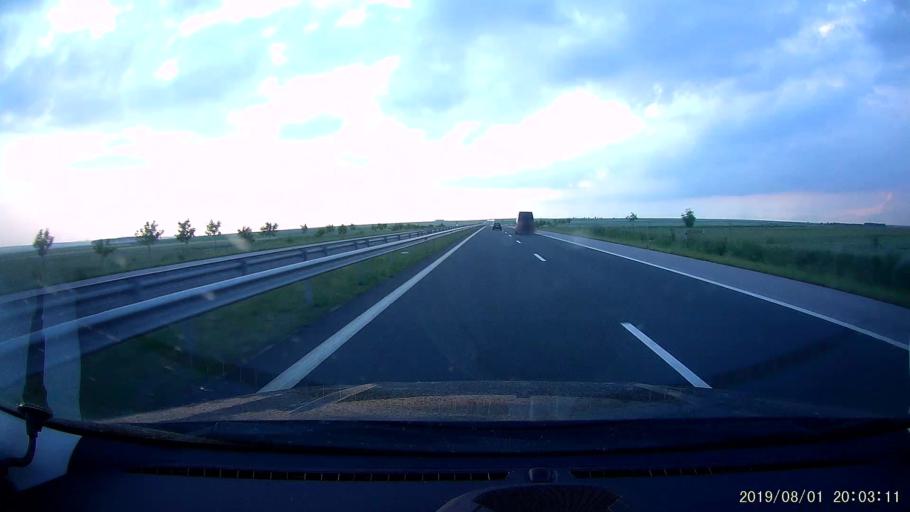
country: BG
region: Yambol
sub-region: Obshtina Straldzha
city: Straldzha
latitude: 42.5584
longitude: 26.6060
